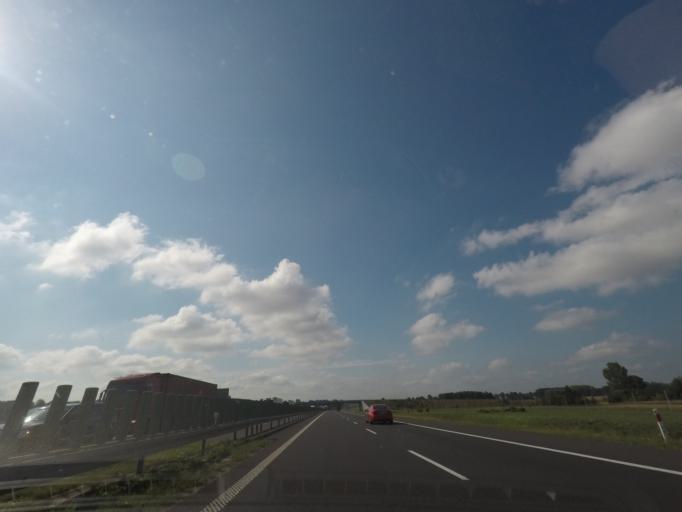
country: PL
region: Pomeranian Voivodeship
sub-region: Powiat starogardzki
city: Smetowo Graniczne
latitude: 53.7189
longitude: 18.6293
